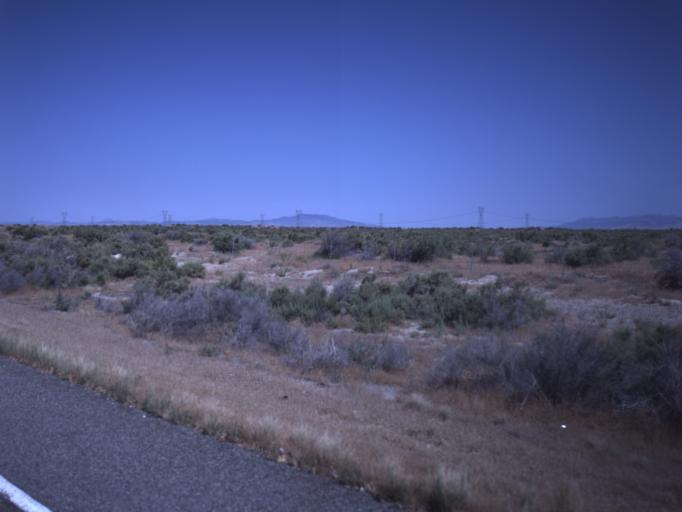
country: US
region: Utah
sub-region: Millard County
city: Delta
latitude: 39.4800
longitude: -112.5073
